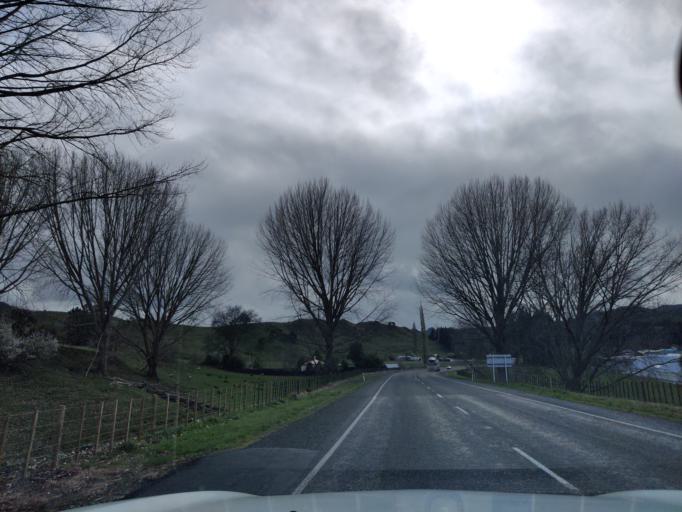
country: NZ
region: Manawatu-Wanganui
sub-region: Ruapehu District
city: Waiouru
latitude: -39.7388
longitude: 175.8401
